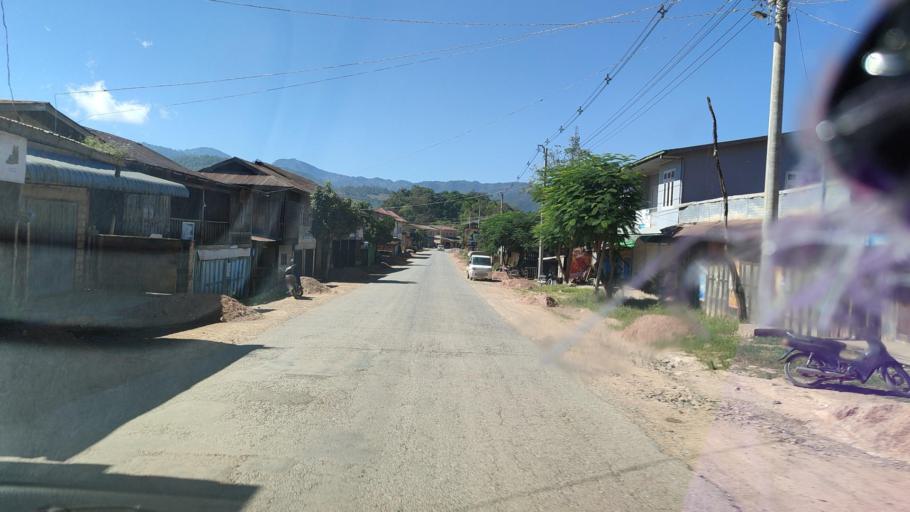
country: MM
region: Shan
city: Taunggyi
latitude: 20.8113
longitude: 97.4561
